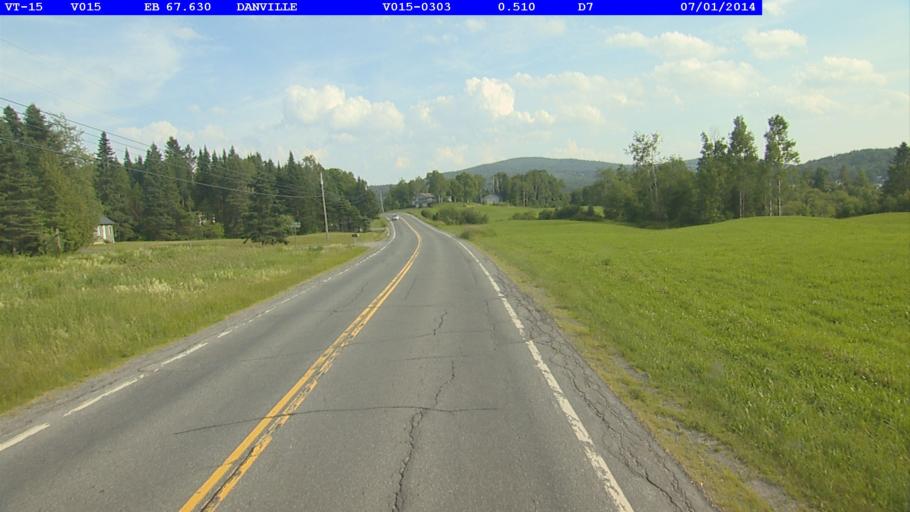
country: US
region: Vermont
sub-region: Caledonia County
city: Hardwick
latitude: 44.4156
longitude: -72.2171
